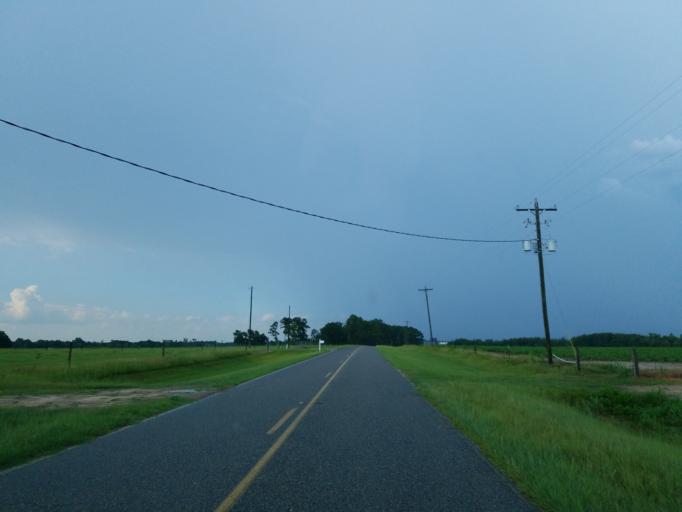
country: US
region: Georgia
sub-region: Cook County
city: Adel
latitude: 31.0708
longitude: -83.4410
